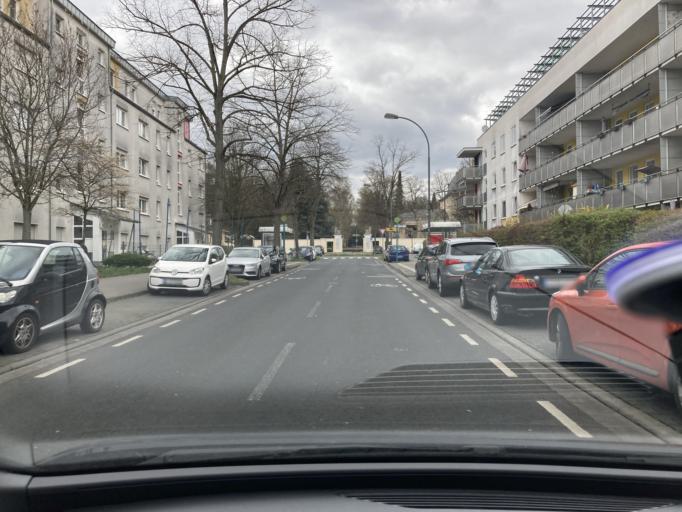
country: DE
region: Hesse
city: Sulzbach
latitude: 50.1141
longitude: 8.5485
